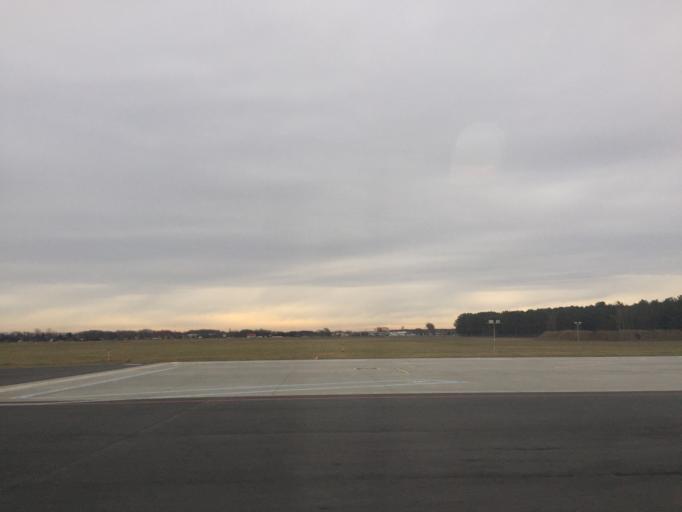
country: PL
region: Kujawsko-Pomorskie
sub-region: Bydgoszcz
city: Bydgoszcz
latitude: 53.0969
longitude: 17.9964
